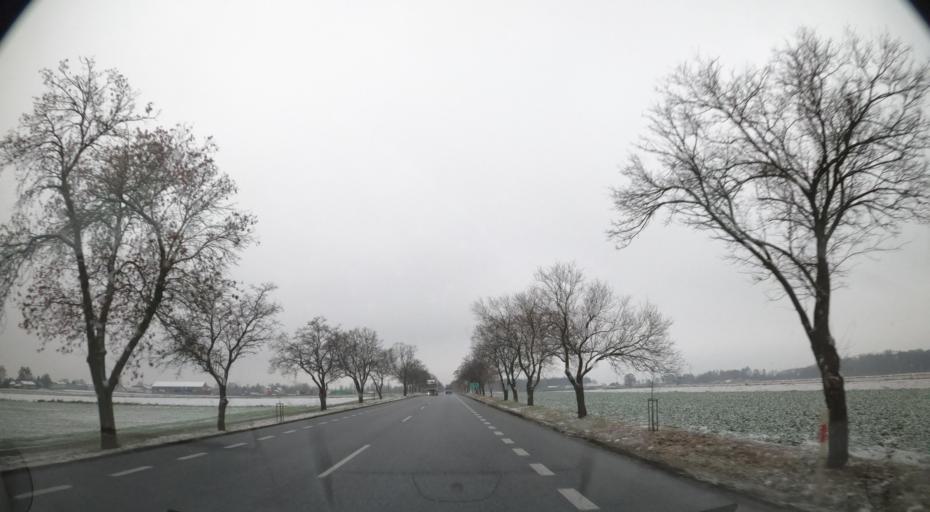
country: PL
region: Masovian Voivodeship
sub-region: Powiat warszawski zachodni
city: Bieniewice
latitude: 52.2022
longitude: 20.5360
